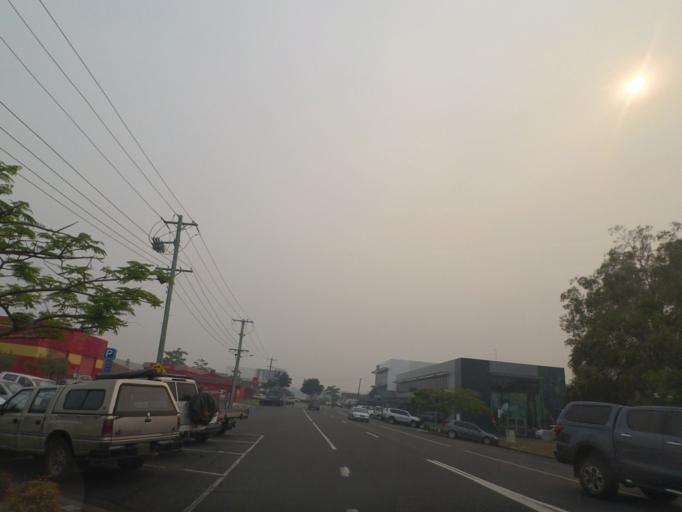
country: AU
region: New South Wales
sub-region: Coffs Harbour
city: Coffs Harbour
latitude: -30.2996
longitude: 153.1147
